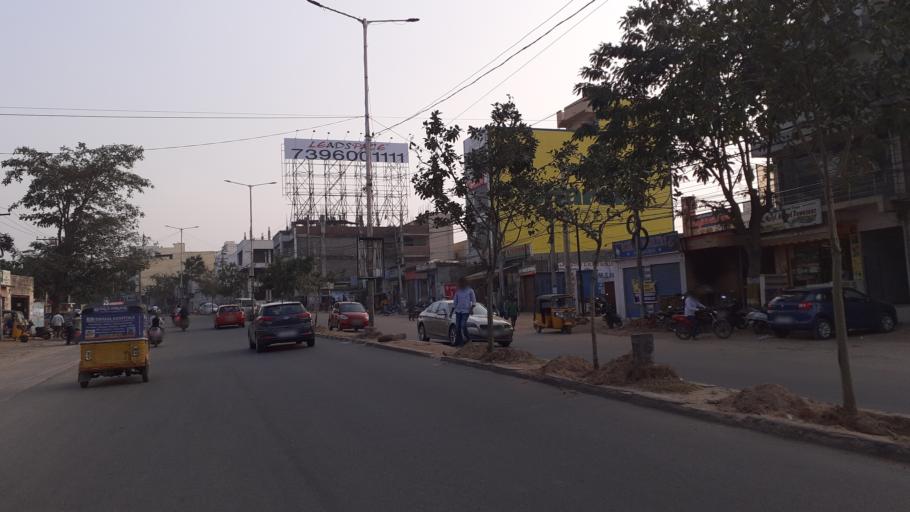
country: IN
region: Telangana
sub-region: Rangareddi
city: Kukatpalli
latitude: 17.4801
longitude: 78.3611
